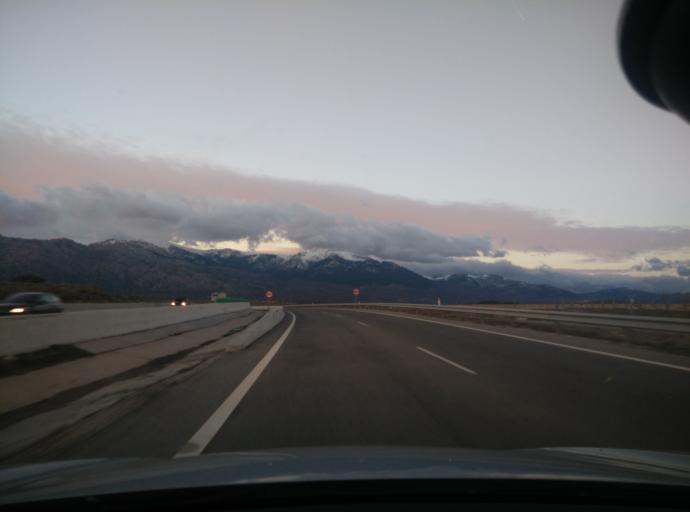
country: ES
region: Madrid
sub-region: Provincia de Madrid
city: Colmenar Viejo
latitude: 40.6985
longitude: -3.7895
